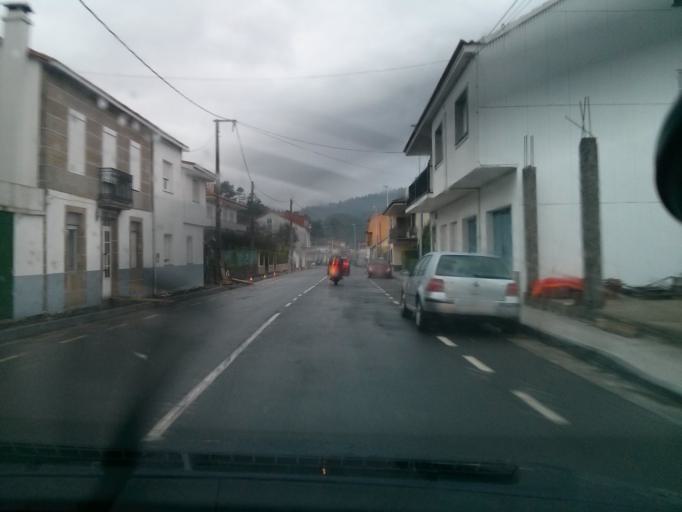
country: ES
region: Galicia
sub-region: Provincia da Coruna
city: Outes
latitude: 42.8303
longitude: -8.8755
